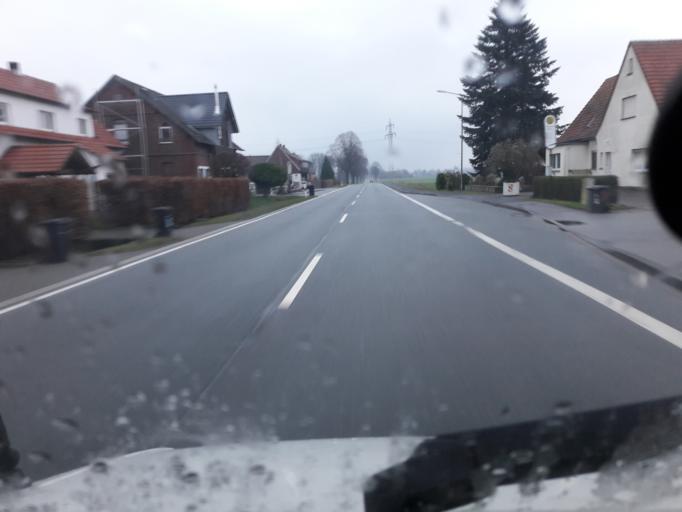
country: DE
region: North Rhine-Westphalia
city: Bad Oeynhausen
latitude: 52.2754
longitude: 8.8383
